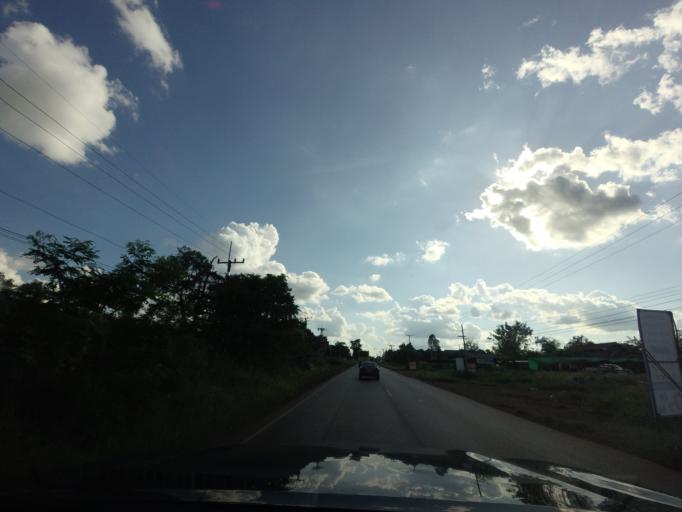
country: TH
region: Changwat Udon Thani
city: Ban Dung
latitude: 17.7402
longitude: 103.2577
